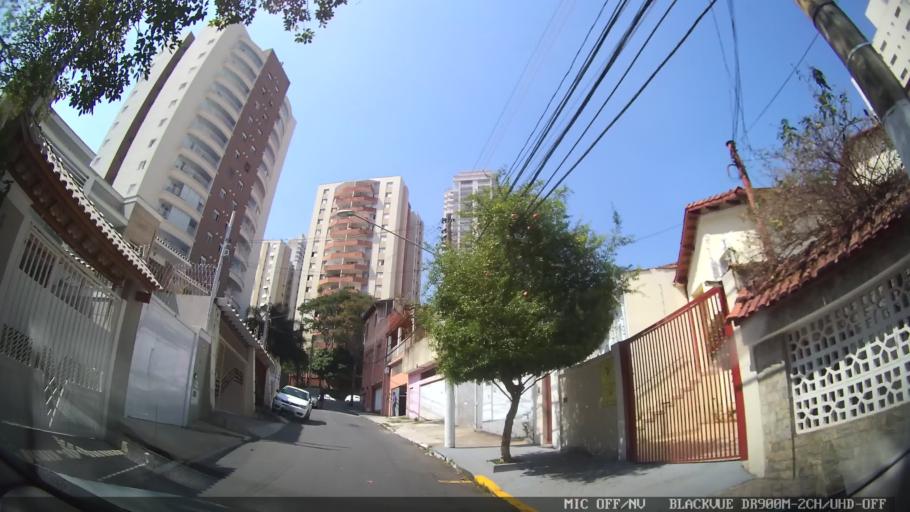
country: BR
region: Sao Paulo
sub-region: Sao Paulo
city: Sao Paulo
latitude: -23.4979
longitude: -46.6329
